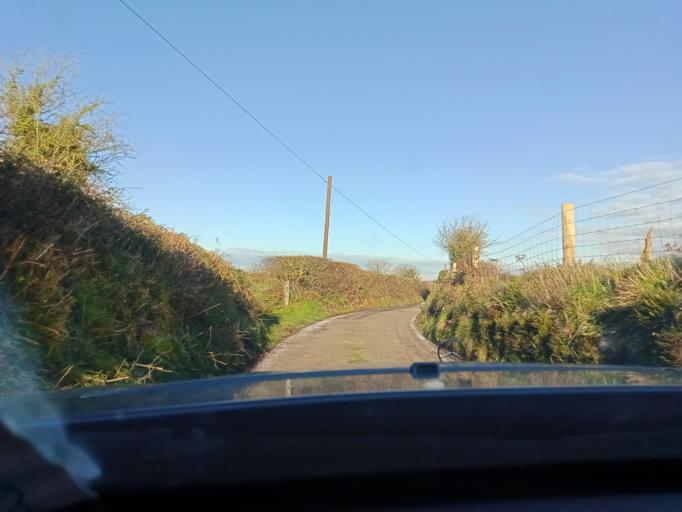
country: IE
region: Leinster
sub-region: Kilkenny
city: Graiguenamanagh
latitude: 52.5589
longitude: -6.9436
